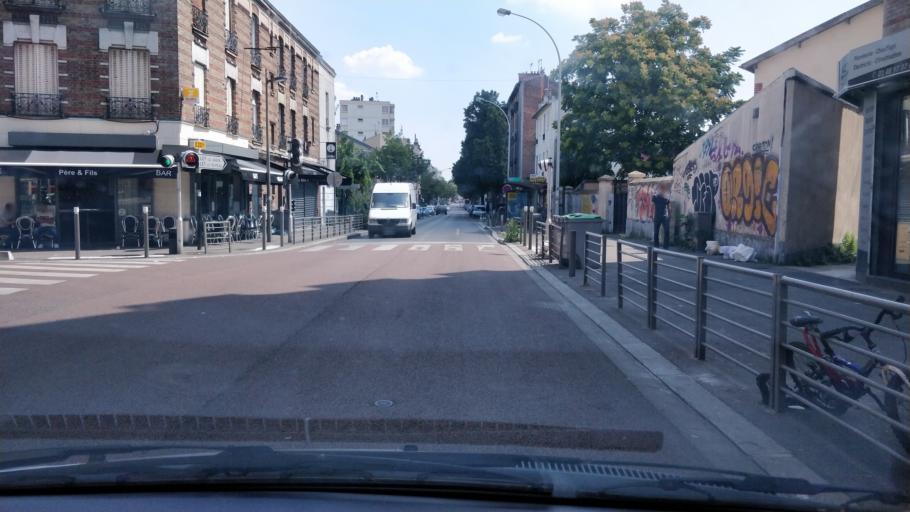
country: FR
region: Ile-de-France
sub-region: Departement de Seine-Saint-Denis
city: Les Lilas
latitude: 48.8760
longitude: 2.4173
